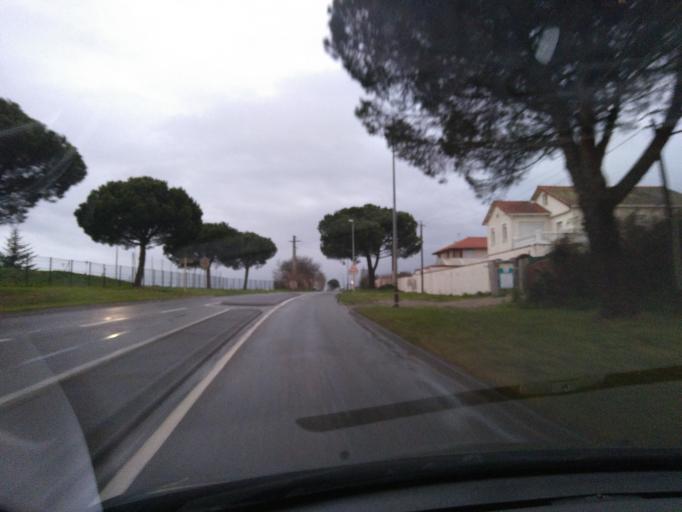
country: FR
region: Midi-Pyrenees
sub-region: Departement de la Haute-Garonne
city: Seilh
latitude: 43.6960
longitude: 1.3505
